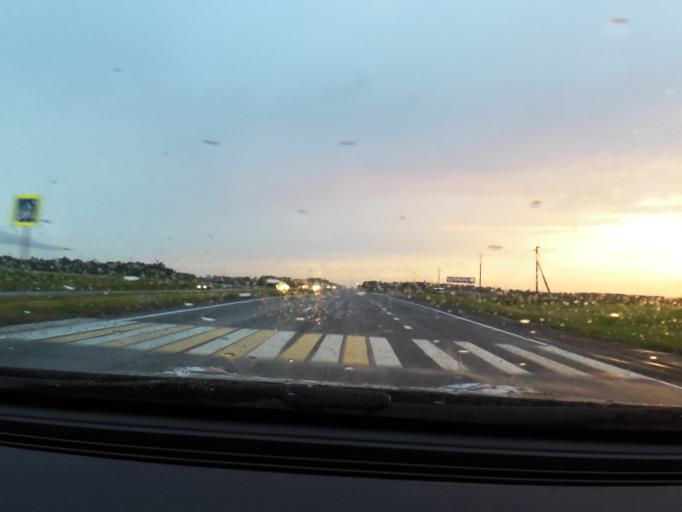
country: RU
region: Tatarstan
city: Yelabuga
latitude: 55.8135
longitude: 52.1175
